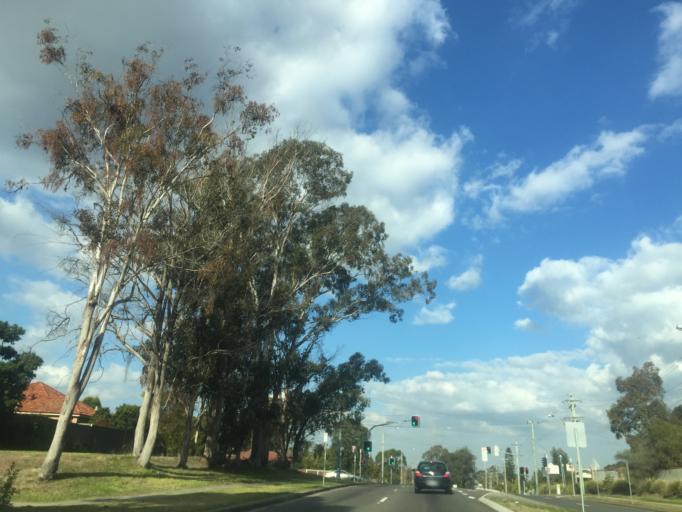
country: AU
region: New South Wales
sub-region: Blacktown
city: Quakers Hill
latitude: -33.7514
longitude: 150.8862
